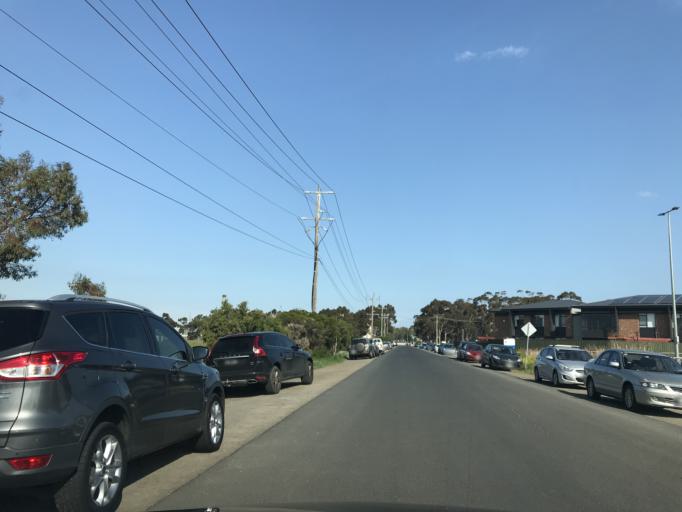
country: AU
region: Victoria
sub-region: Wyndham
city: Hoppers Crossing
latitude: -37.8864
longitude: 144.7020
